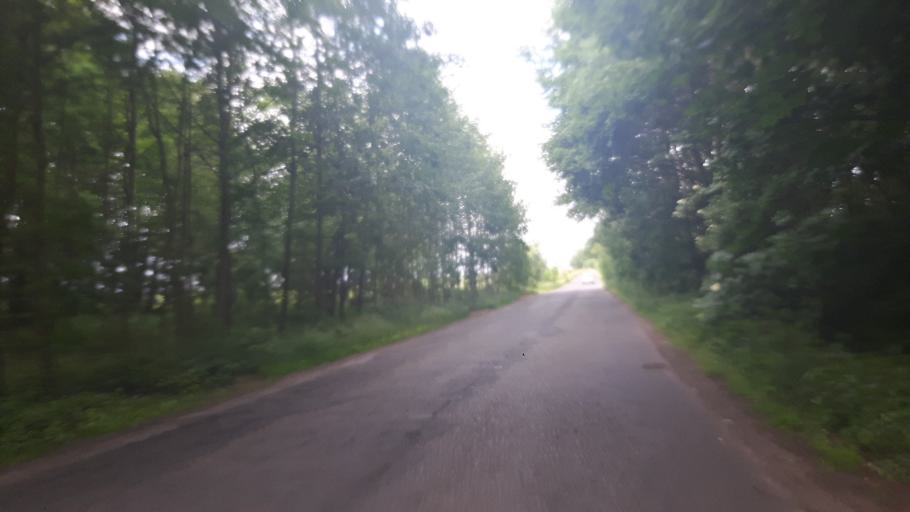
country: DE
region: Brandenburg
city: Rudnitz
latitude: 52.6711
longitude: 13.6484
